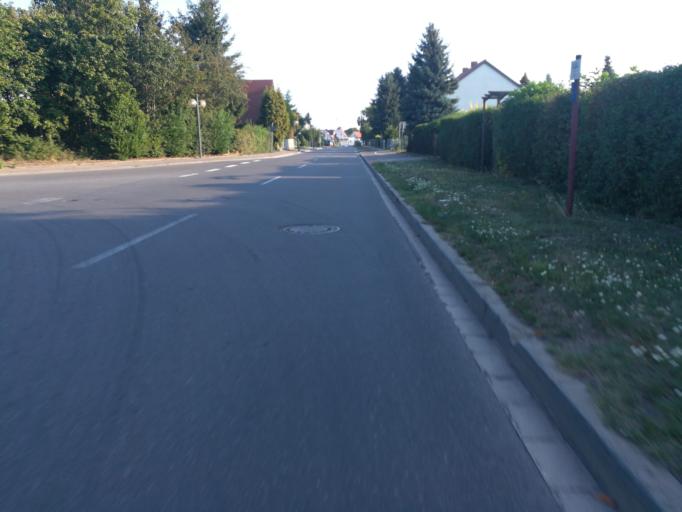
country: DE
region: Saxony-Anhalt
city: Hermsdorf
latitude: 52.1838
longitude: 11.4748
